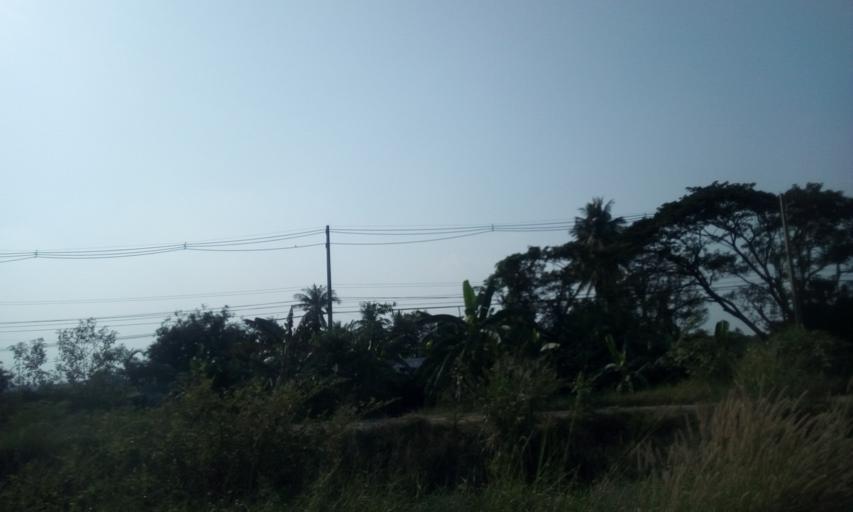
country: TH
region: Sing Buri
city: Phrom Buri
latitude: 14.8350
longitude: 100.4342
